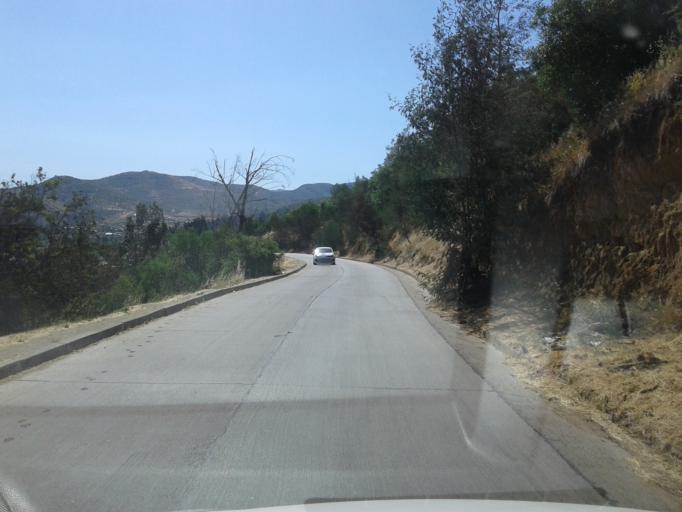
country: CL
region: Valparaiso
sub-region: Provincia de Quillota
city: Quillota
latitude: -32.8755
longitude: -71.2497
